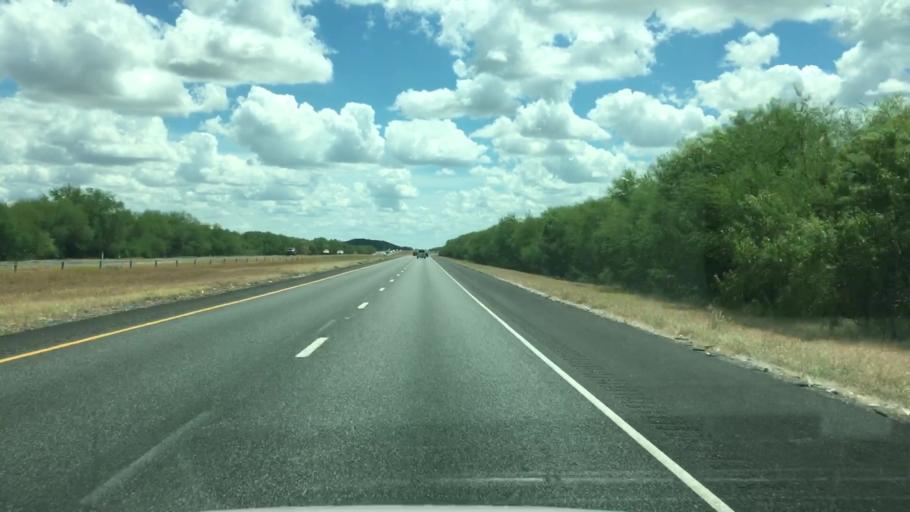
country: US
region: Texas
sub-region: Atascosa County
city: Pleasanton
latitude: 28.7441
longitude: -98.2930
